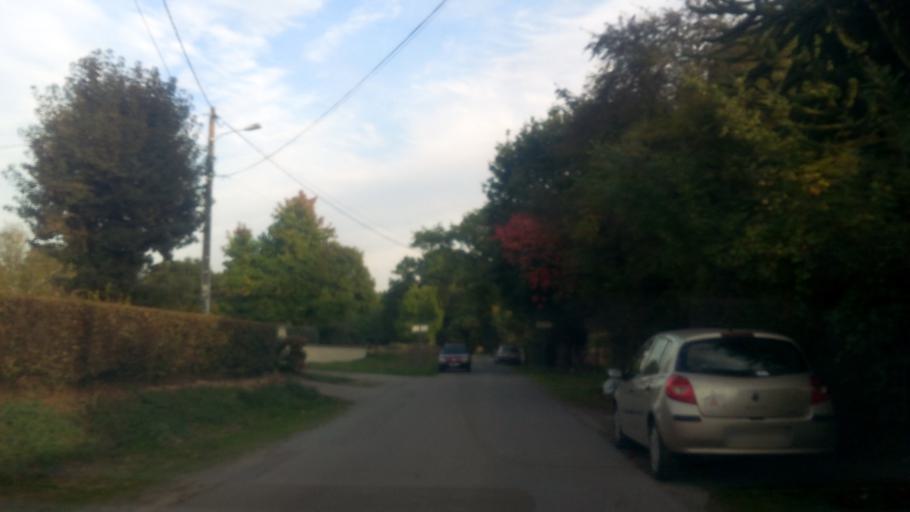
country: FR
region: Pays de la Loire
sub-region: Departement de la Loire-Atlantique
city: Saint-Nicolas-de-Redon
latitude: 47.6570
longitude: -2.0581
